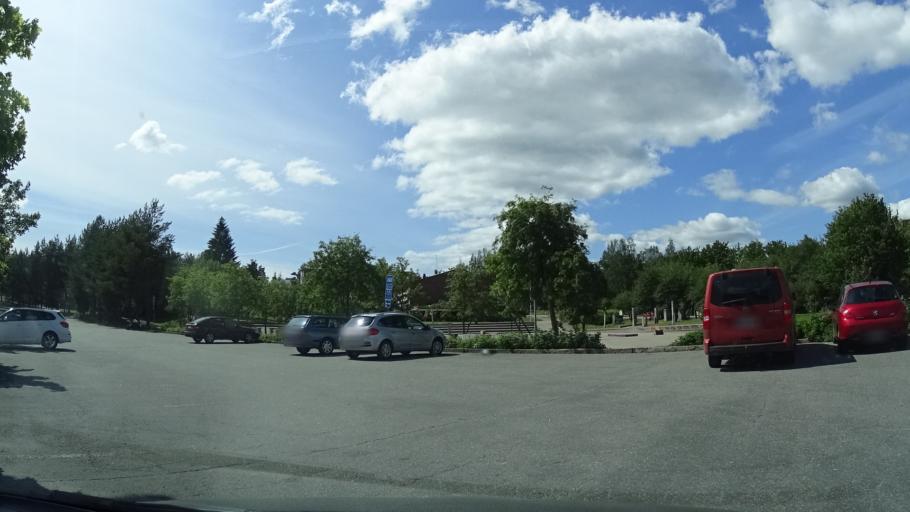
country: FI
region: Central Finland
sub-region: Jyvaeskylae
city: Jyvaeskylae
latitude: 62.2478
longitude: 25.7395
